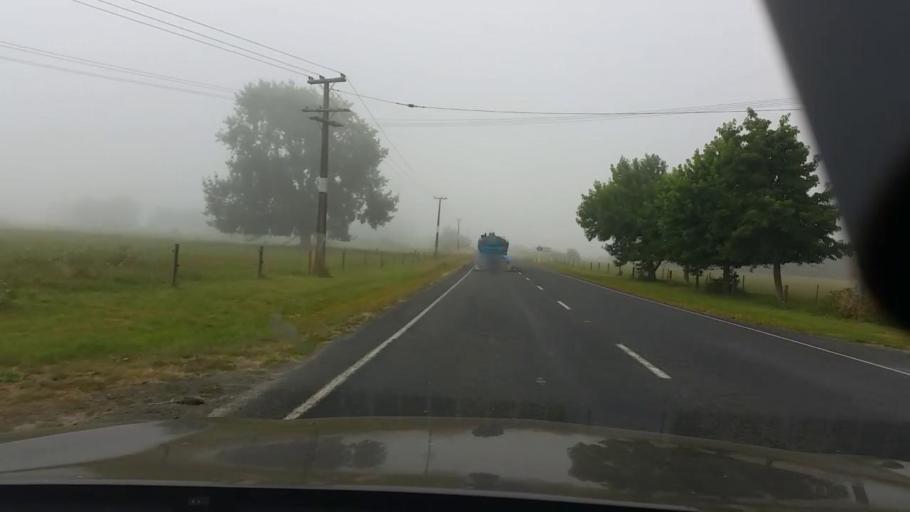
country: NZ
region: Waikato
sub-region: Waikato District
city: Ngaruawahia
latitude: -37.6416
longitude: 175.2948
